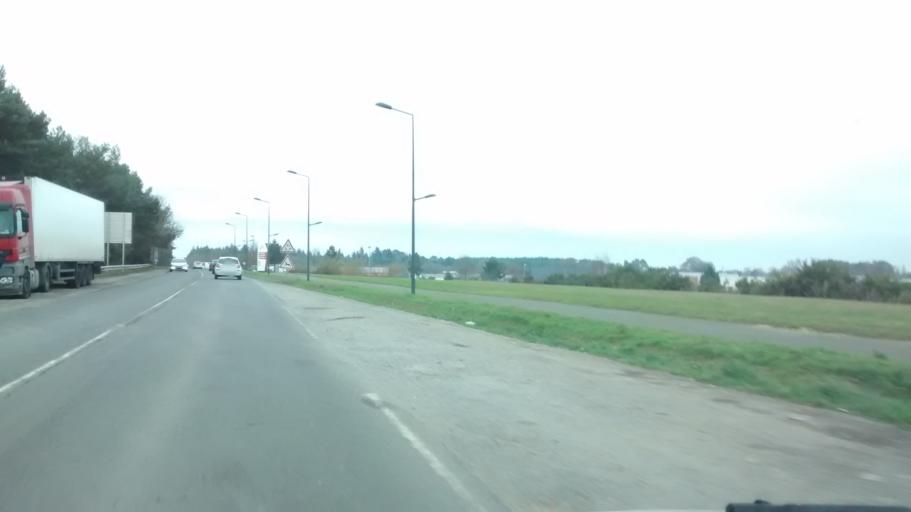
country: FR
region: Brittany
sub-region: Departement d'Ille-et-Vilaine
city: Liffre
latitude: 48.2234
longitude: -1.5009
